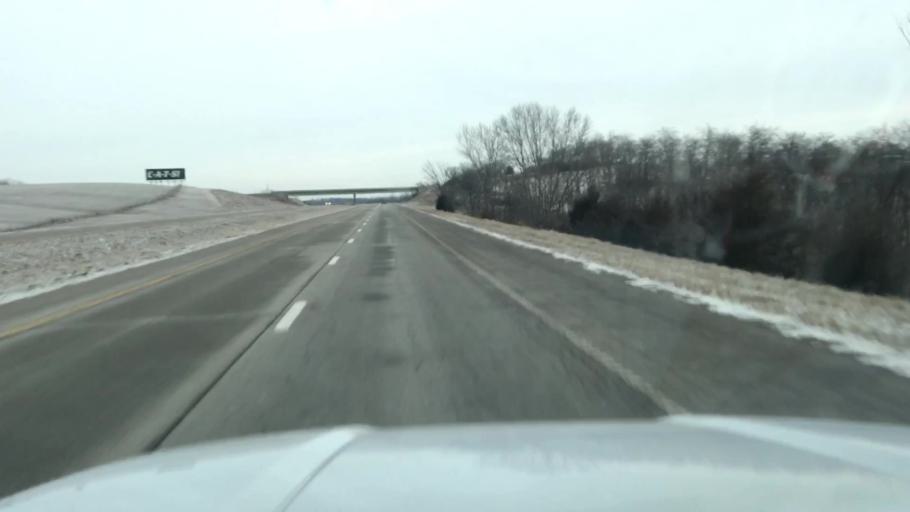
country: US
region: Missouri
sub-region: Andrew County
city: Savannah
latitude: 39.8951
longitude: -94.8570
